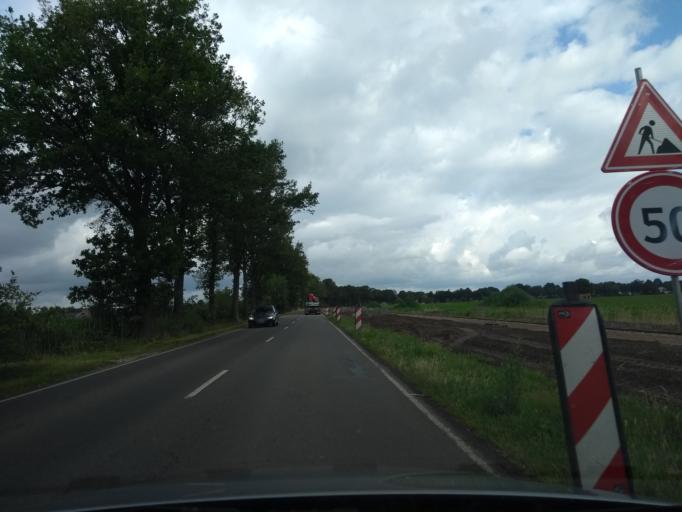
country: NL
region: Overijssel
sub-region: Gemeente Twenterand
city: Vriezenveen
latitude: 52.3928
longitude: 6.6153
